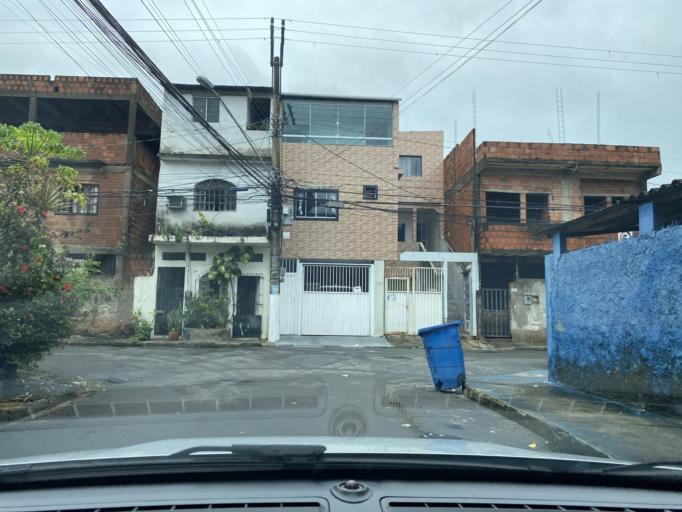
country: BR
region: Espirito Santo
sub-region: Vila Velha
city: Vila Velha
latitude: -20.2554
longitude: -40.2936
